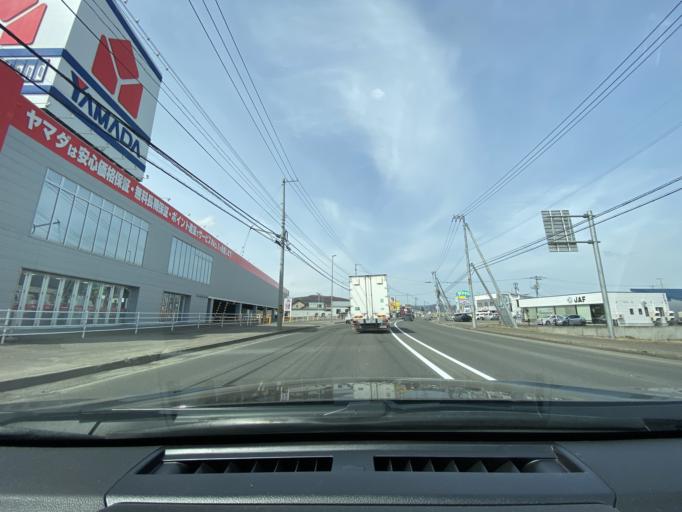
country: JP
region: Hokkaido
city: Kitami
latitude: 43.7967
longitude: 143.8389
